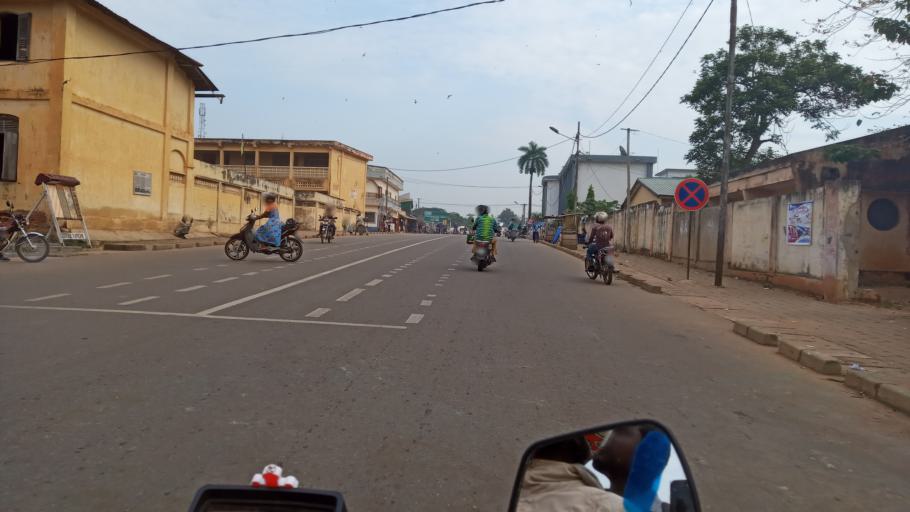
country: TG
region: Plateaux
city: Kpalime
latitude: 6.9049
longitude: 0.6318
